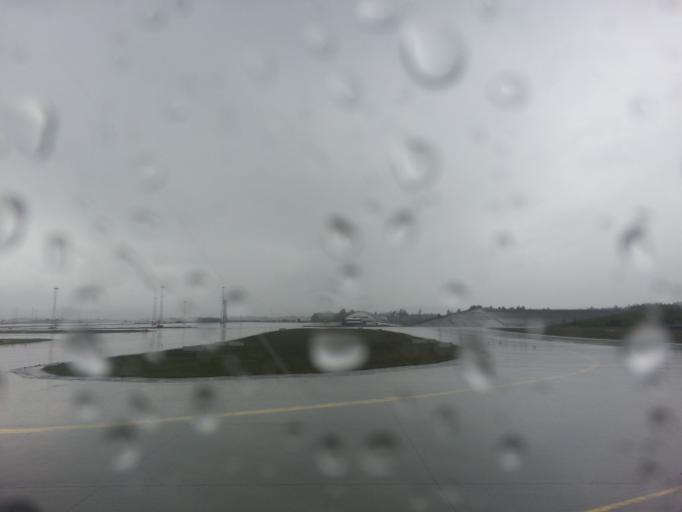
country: NO
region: Akershus
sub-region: Ullensaker
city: Jessheim
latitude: 60.2007
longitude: 11.1221
